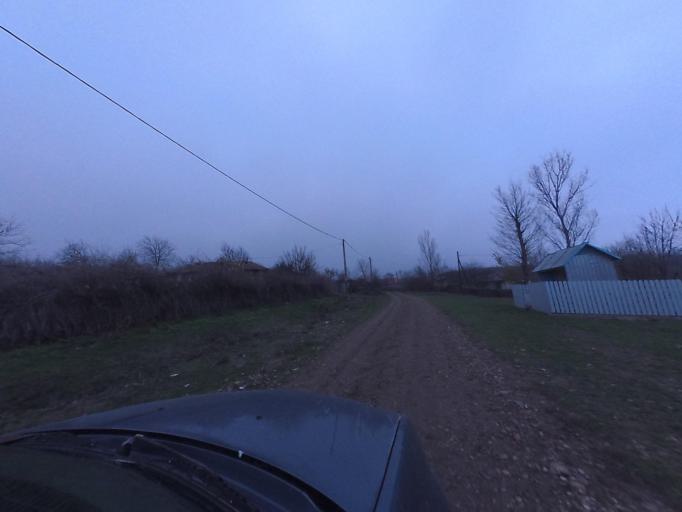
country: RO
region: Galati
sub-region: Comuna Balabanesti
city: Balabanesti
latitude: 46.1427
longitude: 27.7451
